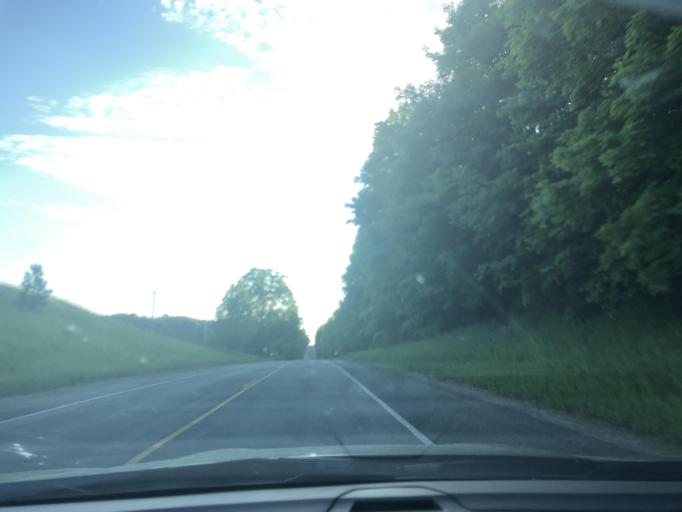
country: US
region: Michigan
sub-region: Missaukee County
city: Lake City
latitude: 44.4668
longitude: -85.1008
